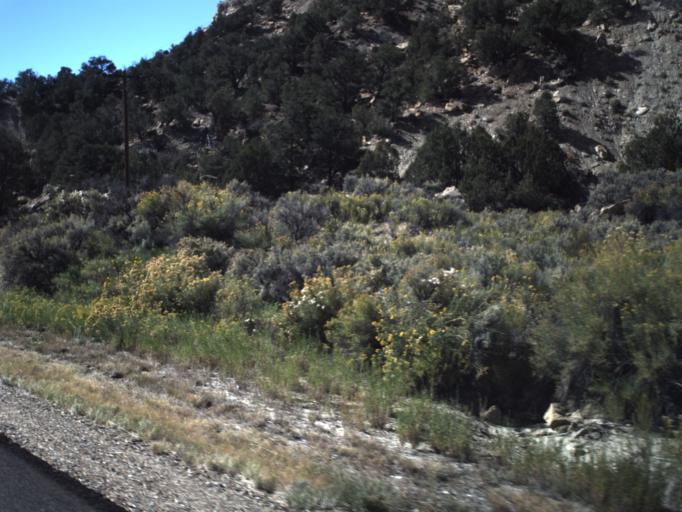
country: US
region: Utah
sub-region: Garfield County
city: Panguitch
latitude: 37.6074
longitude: -111.9056
